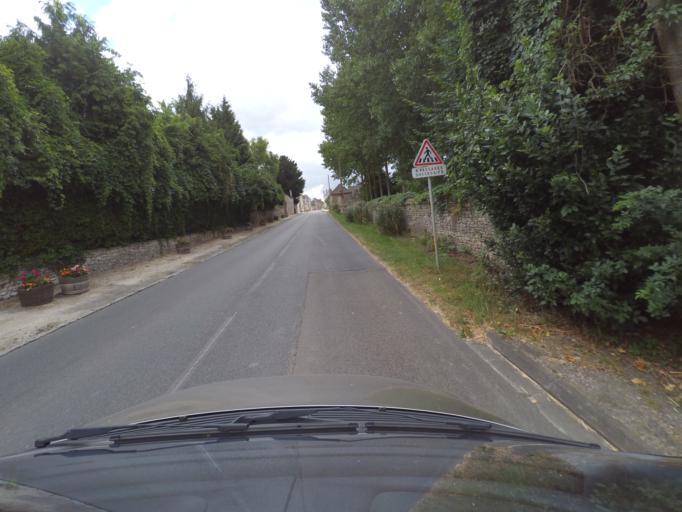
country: FR
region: Poitou-Charentes
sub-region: Departement de la Vienne
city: Saint-Gervais-les-Trois-Clochers
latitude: 46.9495
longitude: 0.4125
